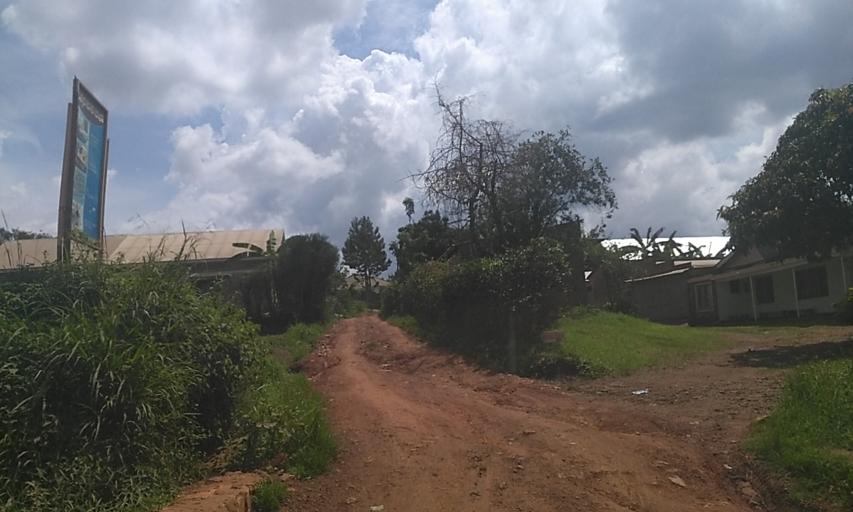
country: UG
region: Central Region
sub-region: Wakiso District
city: Wakiso
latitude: 0.3963
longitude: 32.4744
